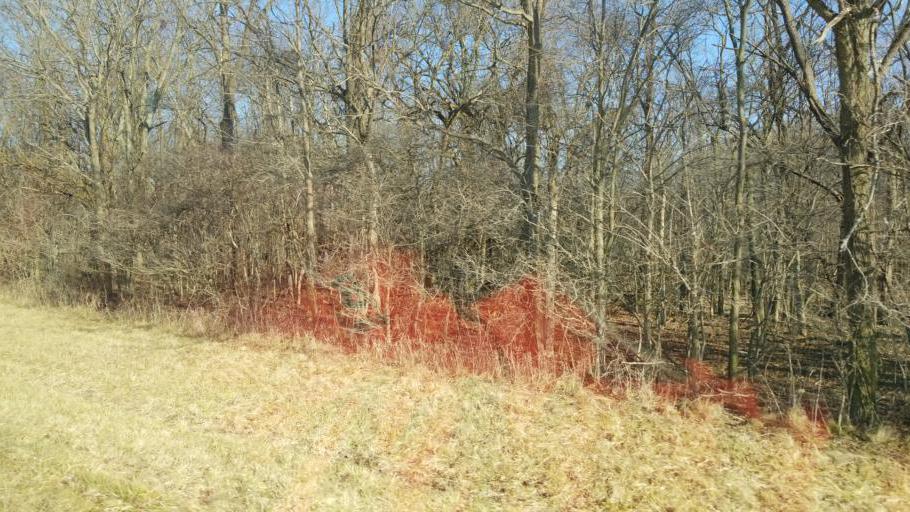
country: US
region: Ohio
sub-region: Crawford County
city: Bucyrus
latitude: 40.9340
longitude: -83.0741
